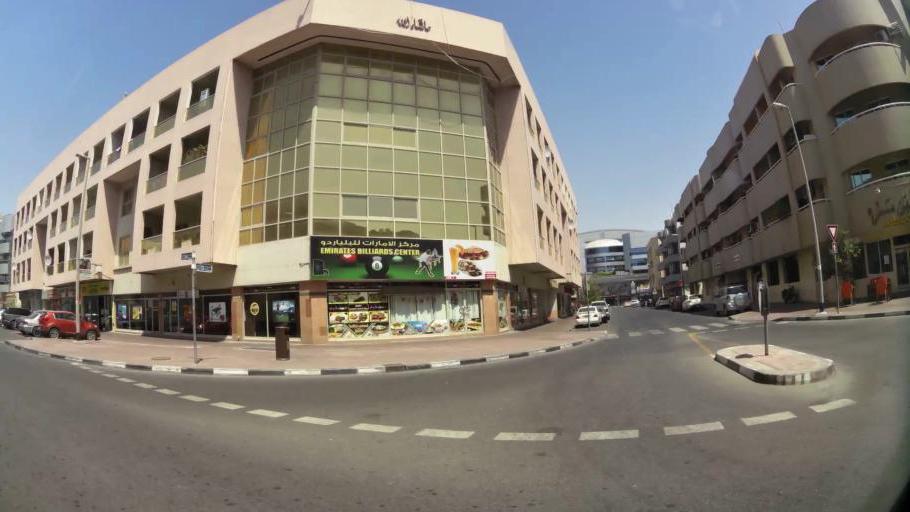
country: AE
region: Ash Shariqah
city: Sharjah
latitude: 25.2810
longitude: 55.3525
